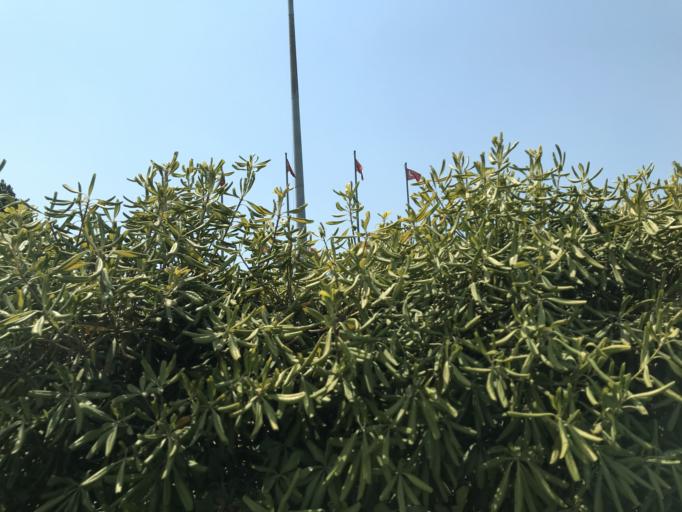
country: TR
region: Aydin
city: Ortaklar
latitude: 37.8838
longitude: 27.5055
